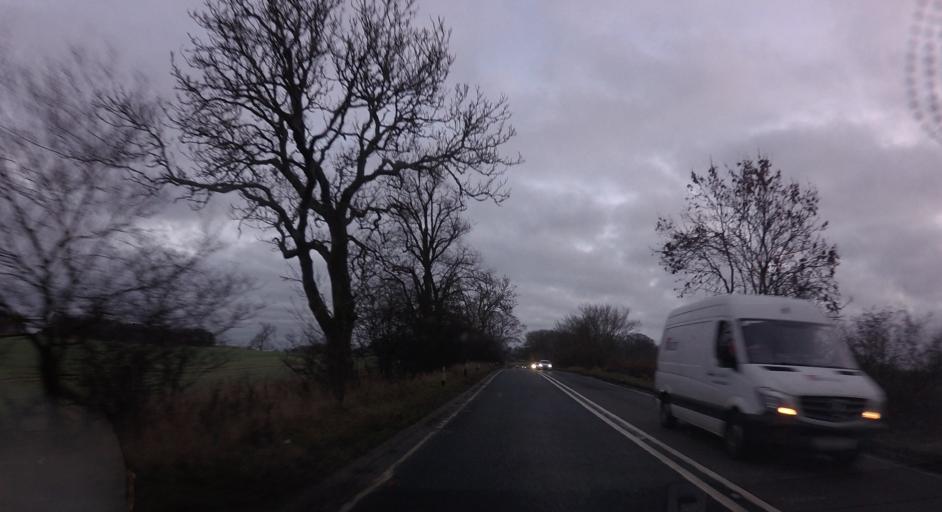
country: GB
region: Scotland
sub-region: Fife
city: Limekilns
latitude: 56.0446
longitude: -3.4747
